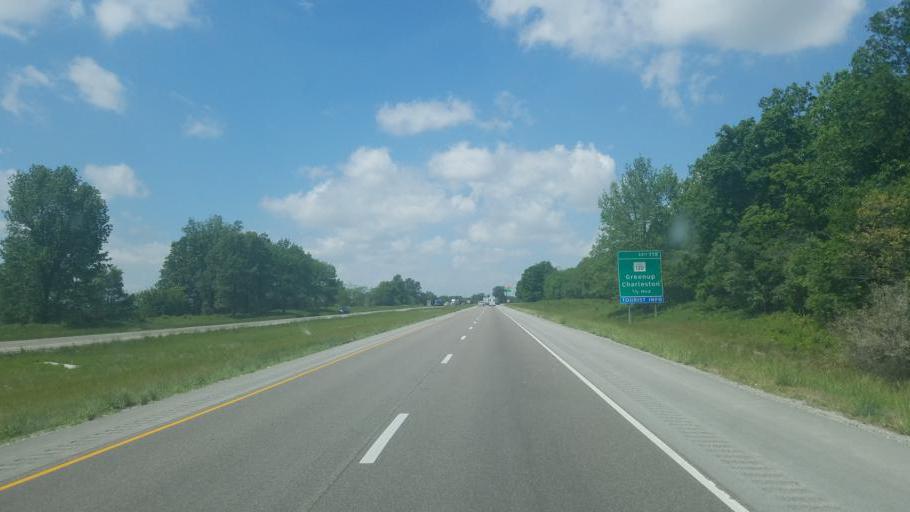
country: US
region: Illinois
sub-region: Cumberland County
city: Greenup
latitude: 39.2579
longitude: -88.1392
